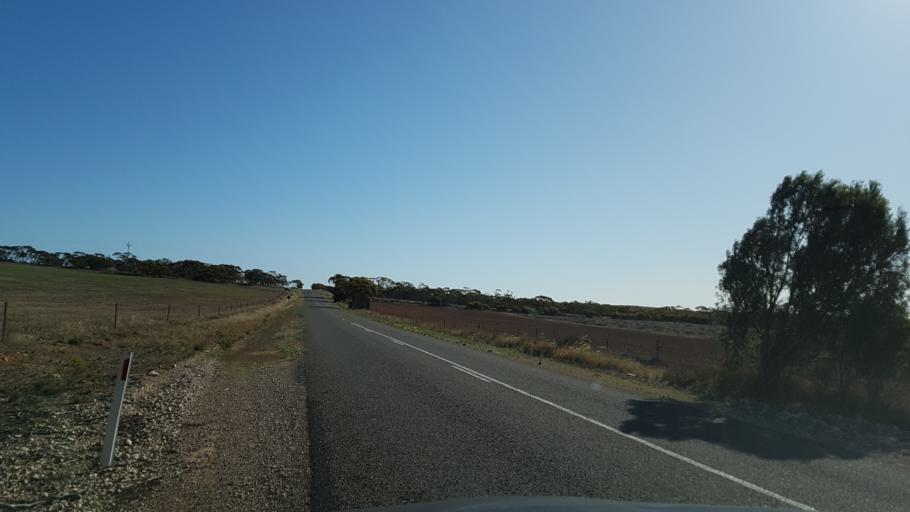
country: AU
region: South Australia
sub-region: Mid Murray
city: Mannum
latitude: -34.7800
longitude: 139.5312
